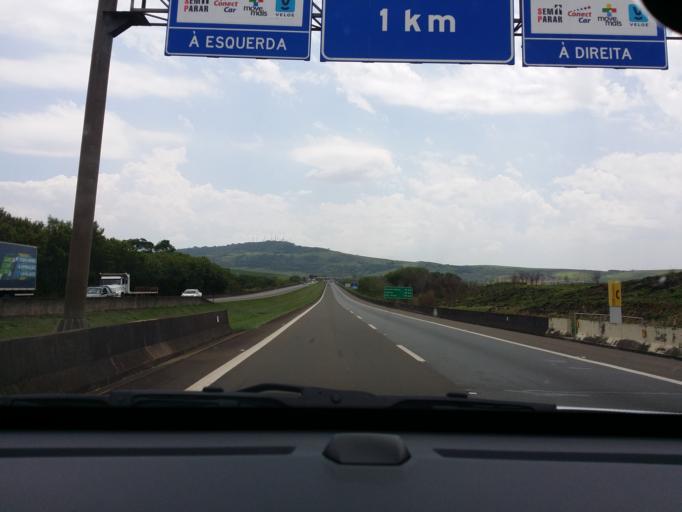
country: BR
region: Sao Paulo
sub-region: Limeira
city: Limeira
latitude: -22.5665
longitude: -47.4575
